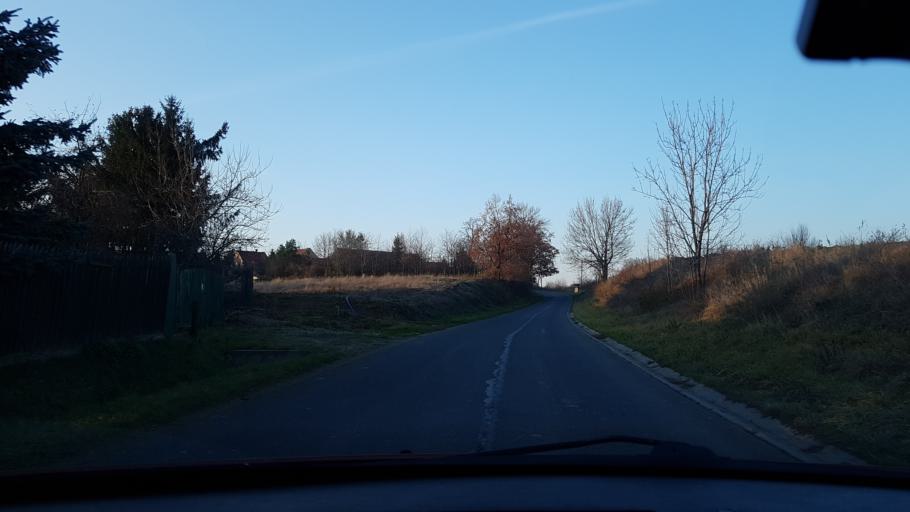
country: PL
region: Lower Silesian Voivodeship
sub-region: Powiat zabkowicki
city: Henrykow
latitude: 50.6649
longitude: 16.9848
